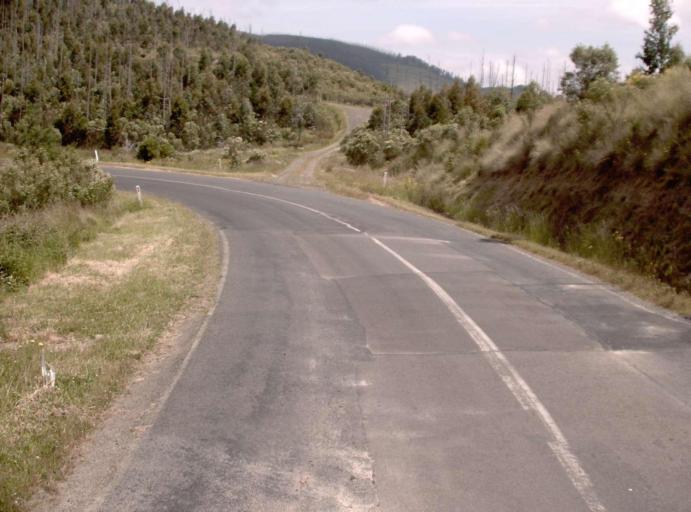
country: AU
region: Victoria
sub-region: Latrobe
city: Traralgon
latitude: -38.3707
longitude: 146.5661
